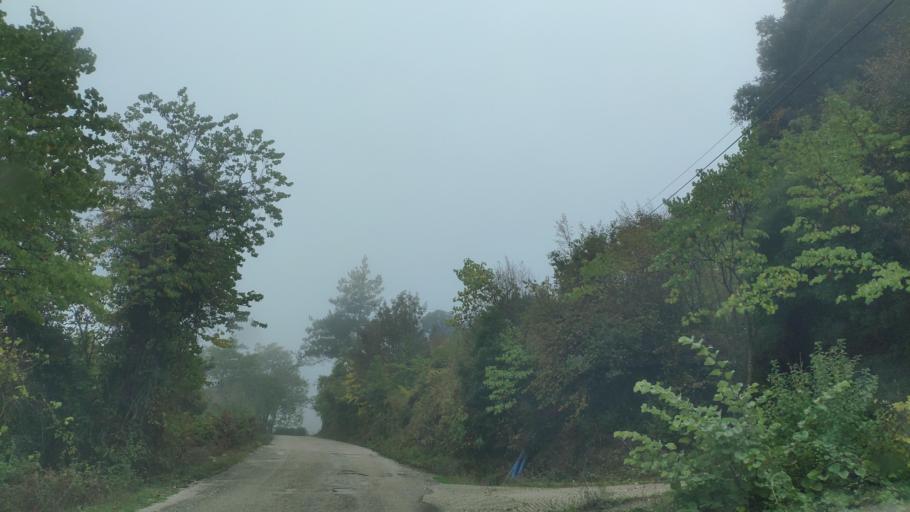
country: GR
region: Epirus
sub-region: Nomos Thesprotias
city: Paramythia
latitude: 39.4660
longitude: 20.6717
